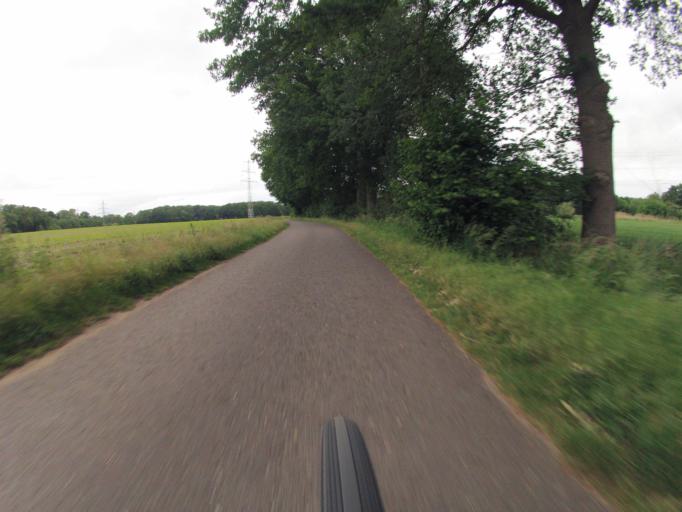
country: DE
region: North Rhine-Westphalia
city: Emsdetten
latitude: 52.2230
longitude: 7.5187
